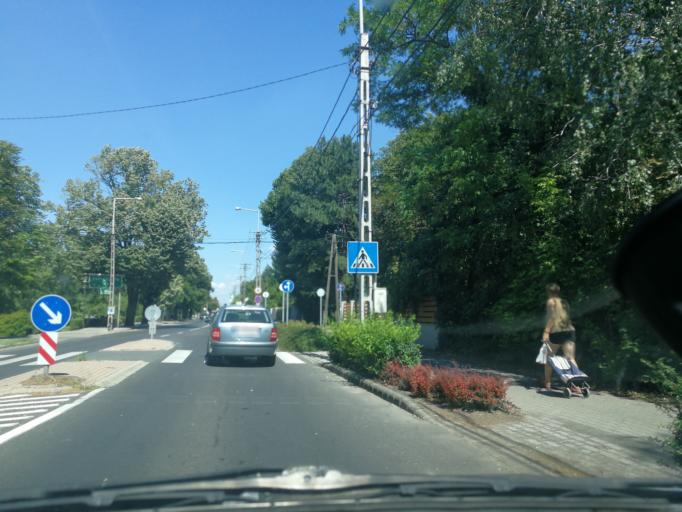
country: HU
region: Fejer
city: Gardony
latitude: 47.1960
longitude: 18.6062
